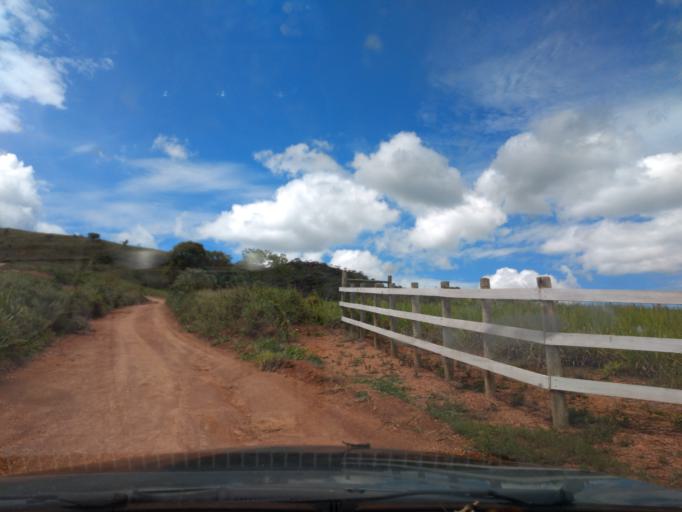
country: BR
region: Minas Gerais
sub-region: Lavras
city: Lavras
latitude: -21.5222
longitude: -44.9303
